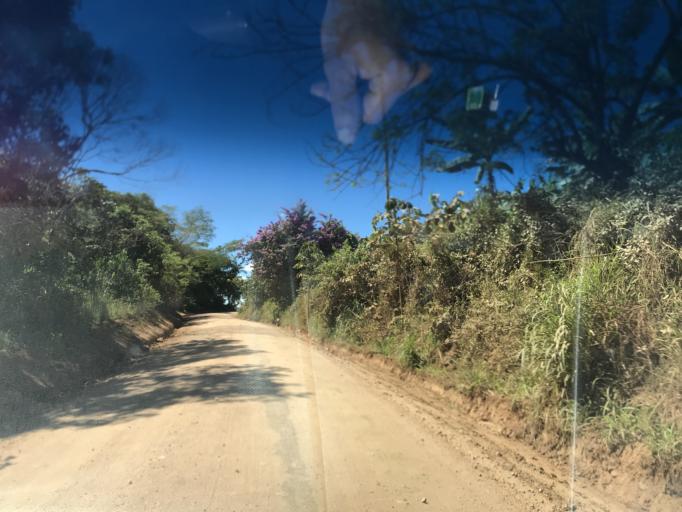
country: BR
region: Bahia
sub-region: Mutuipe
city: Mutuipe
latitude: -13.3722
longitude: -39.3724
